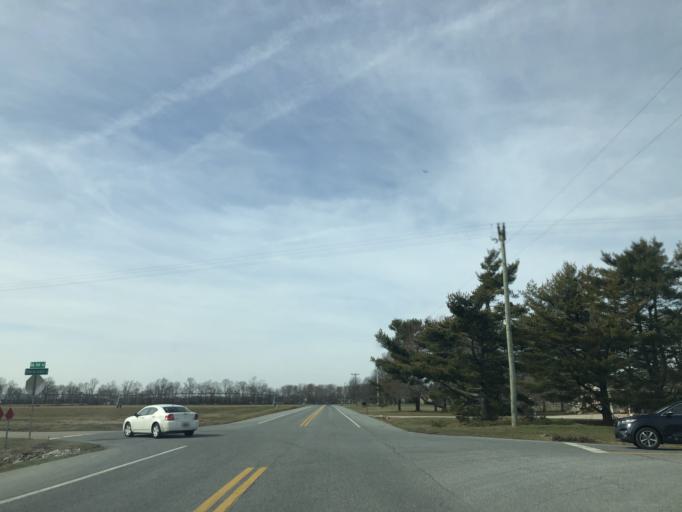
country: US
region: Delaware
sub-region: Kent County
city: Smyrna
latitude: 39.2820
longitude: -75.5699
